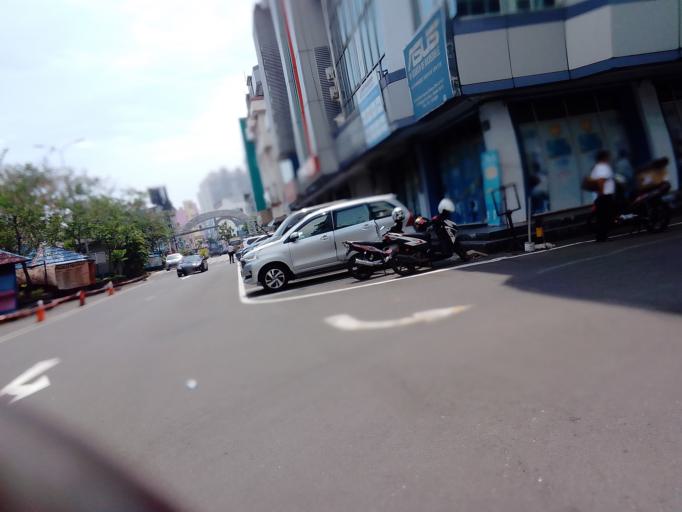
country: ID
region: Jakarta Raya
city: Jakarta
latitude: -6.1369
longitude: 106.8292
